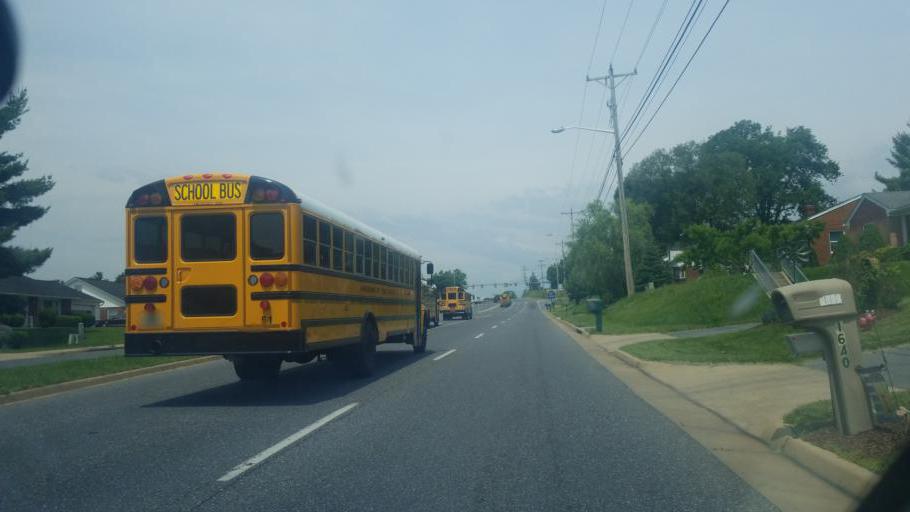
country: US
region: Virginia
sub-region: City of Harrisonburg
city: Harrisonburg
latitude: 38.4546
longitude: -78.8966
